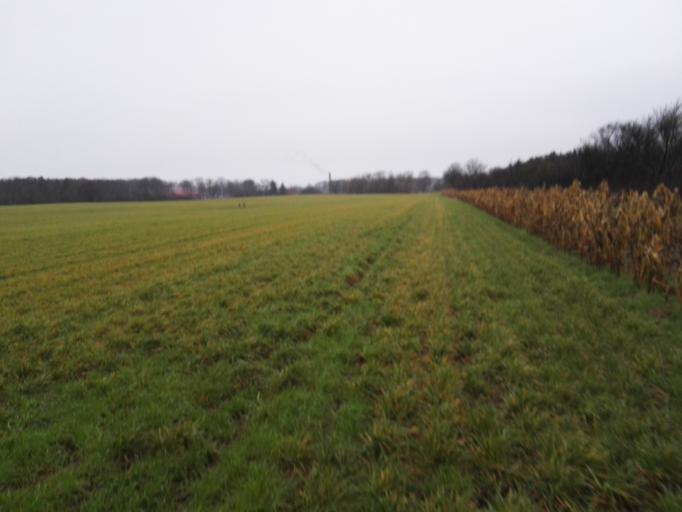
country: DK
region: Capital Region
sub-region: Frederikssund Kommune
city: Jaegerspris
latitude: 55.8504
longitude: 11.9736
